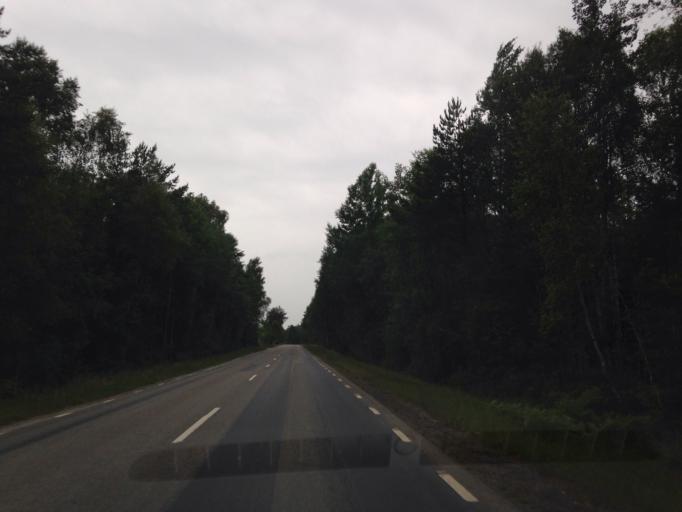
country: SE
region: Vaestra Goetaland
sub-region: Harryda Kommun
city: Hindas
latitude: 57.6740
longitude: 12.3443
